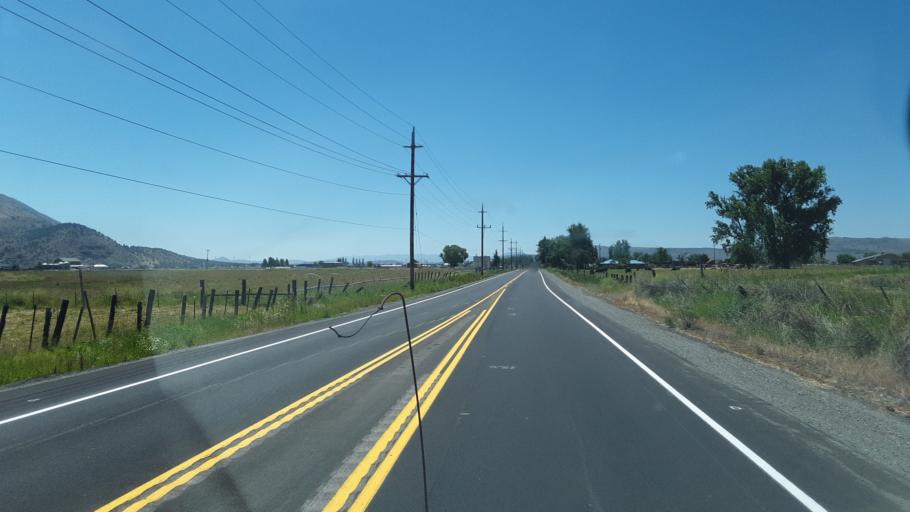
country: US
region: Oregon
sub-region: Klamath County
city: Altamont
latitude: 42.1621
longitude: -121.6982
